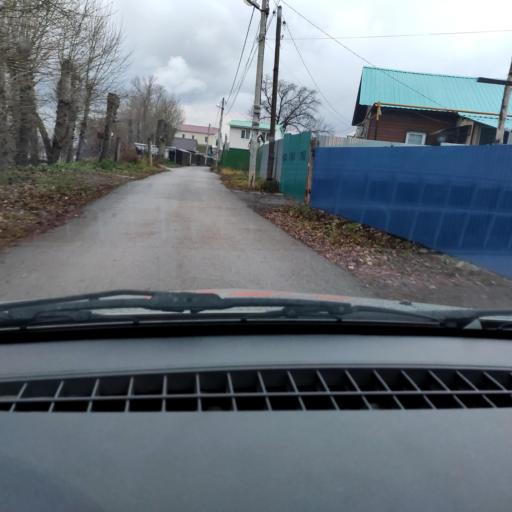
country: RU
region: Bashkortostan
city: Ufa
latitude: 54.7331
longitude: 55.9114
